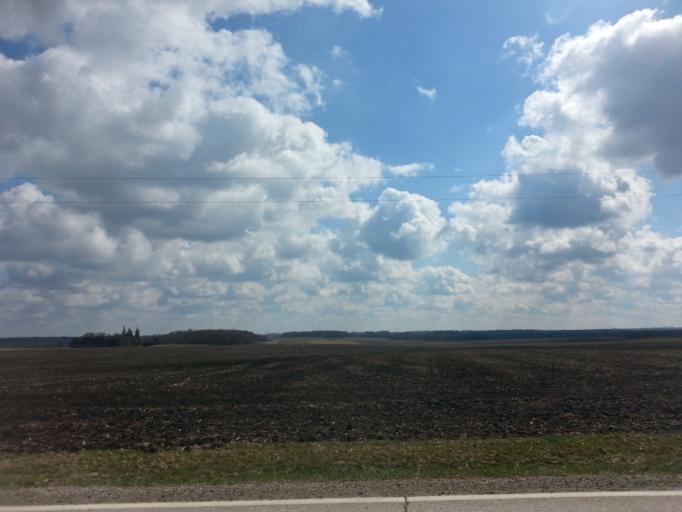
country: US
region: Minnesota
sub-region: Dodge County
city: Mantorville
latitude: 44.0943
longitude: -92.6967
